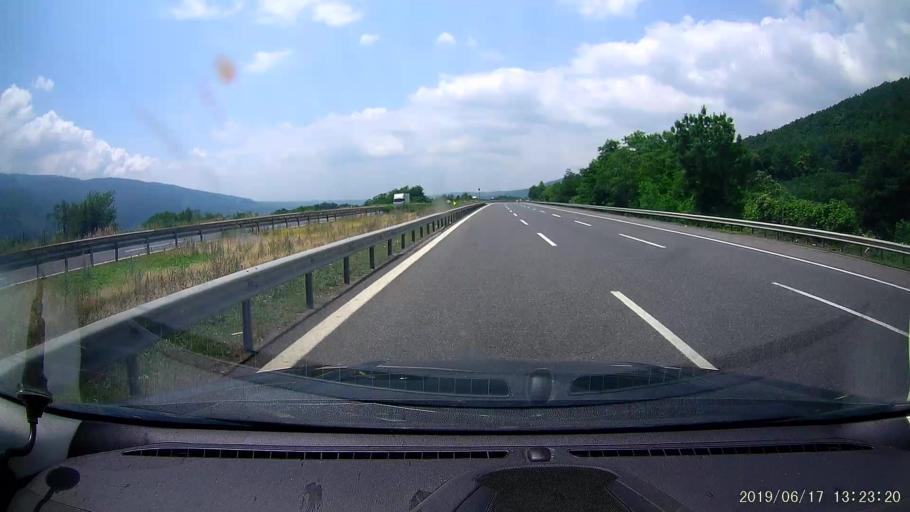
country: TR
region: Duzce
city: Gumusova
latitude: 40.8092
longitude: 30.8849
